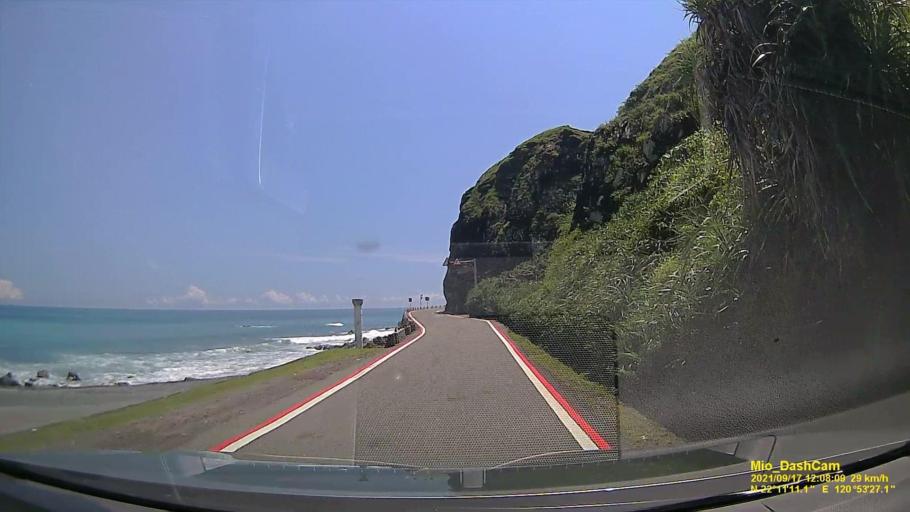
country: TW
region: Taiwan
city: Hengchun
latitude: 22.1864
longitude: 120.8909
